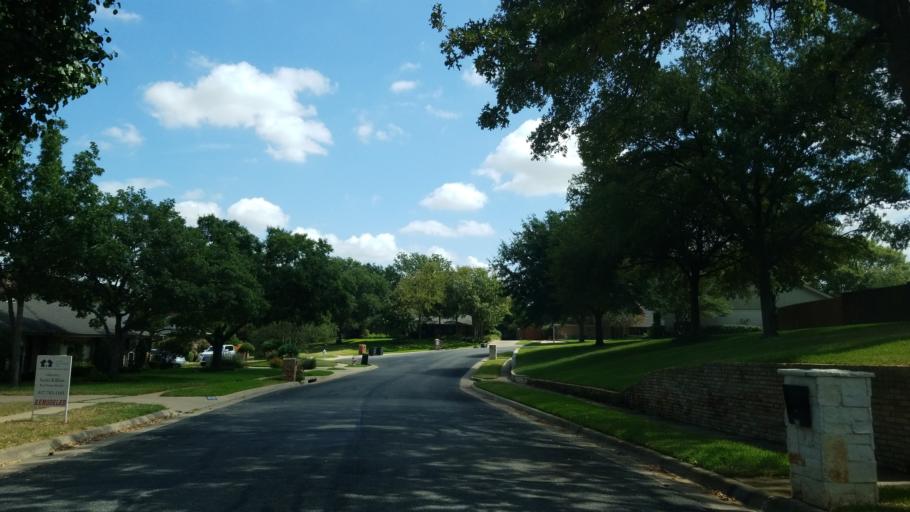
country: US
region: Texas
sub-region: Tarrant County
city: Euless
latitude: 32.8646
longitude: -97.0926
